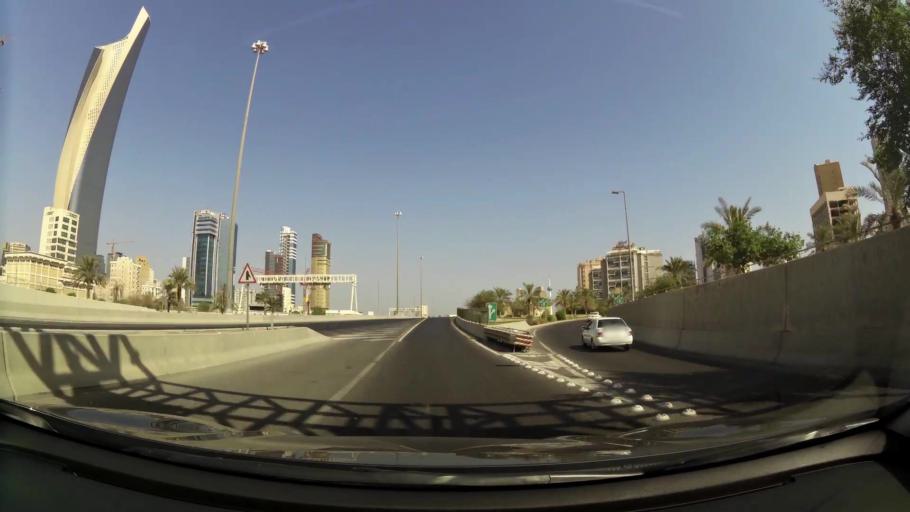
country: KW
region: Al Asimah
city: Ad Dasmah
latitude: 29.3754
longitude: 47.9972
